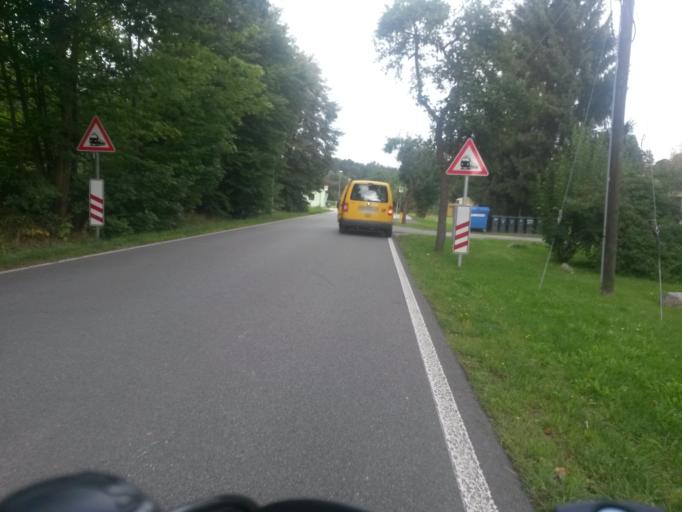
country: DE
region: Brandenburg
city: Angermunde
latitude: 53.0519
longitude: 13.9445
